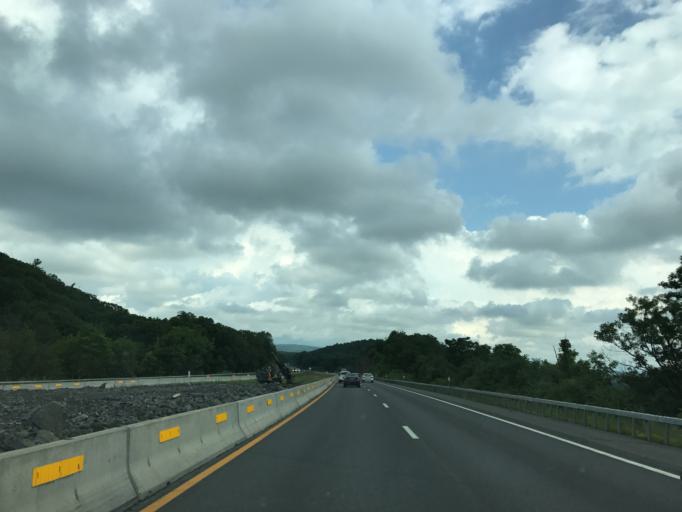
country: US
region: New York
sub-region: Greene County
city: Jefferson Heights
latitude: 42.2790
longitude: -73.8724
